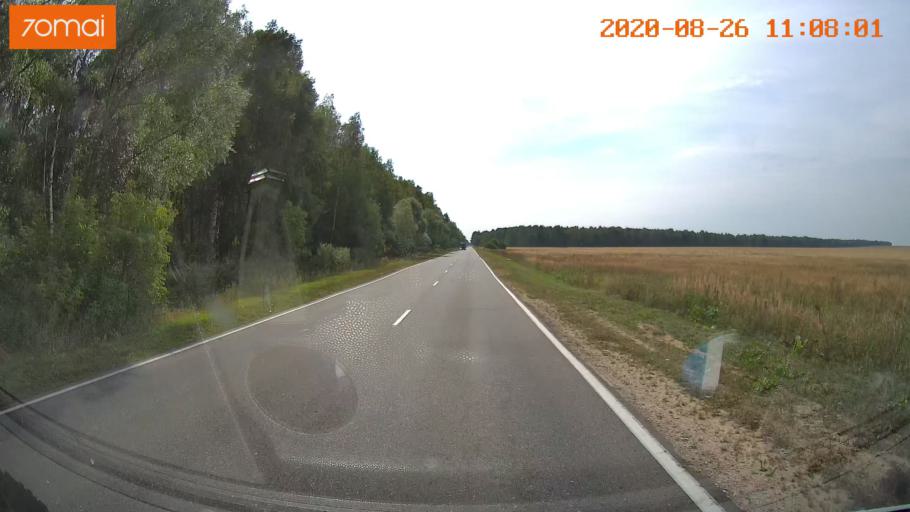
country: RU
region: Rjazan
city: Izhevskoye
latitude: 54.5109
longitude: 41.1213
